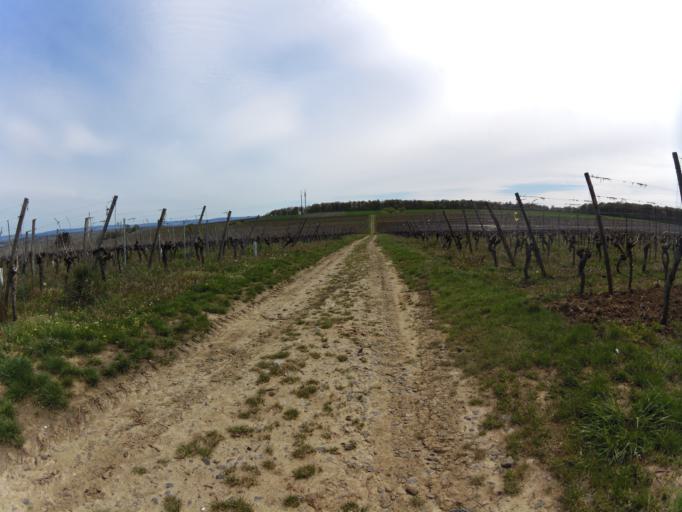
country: DE
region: Bavaria
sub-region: Regierungsbezirk Unterfranken
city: Nordheim
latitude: 49.8633
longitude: 10.1609
